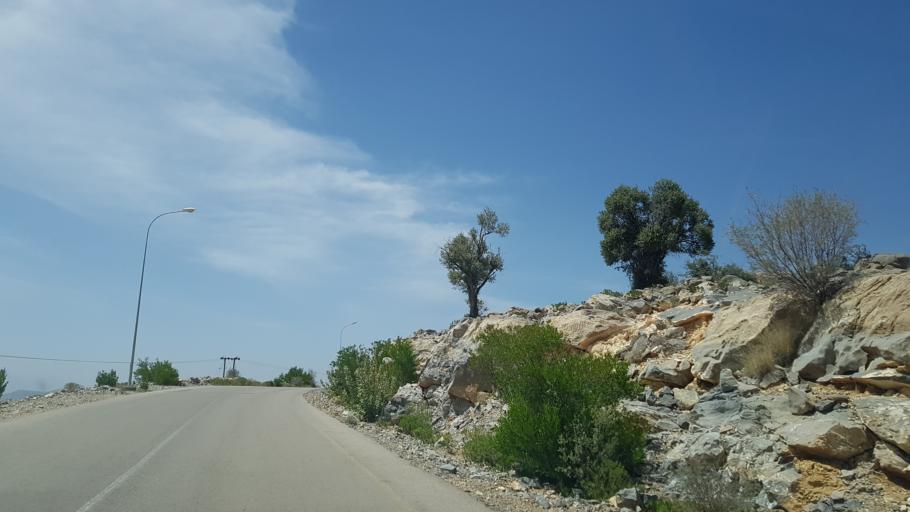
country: OM
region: Al Batinah
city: Bayt al `Awabi
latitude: 23.1249
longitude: 57.6004
